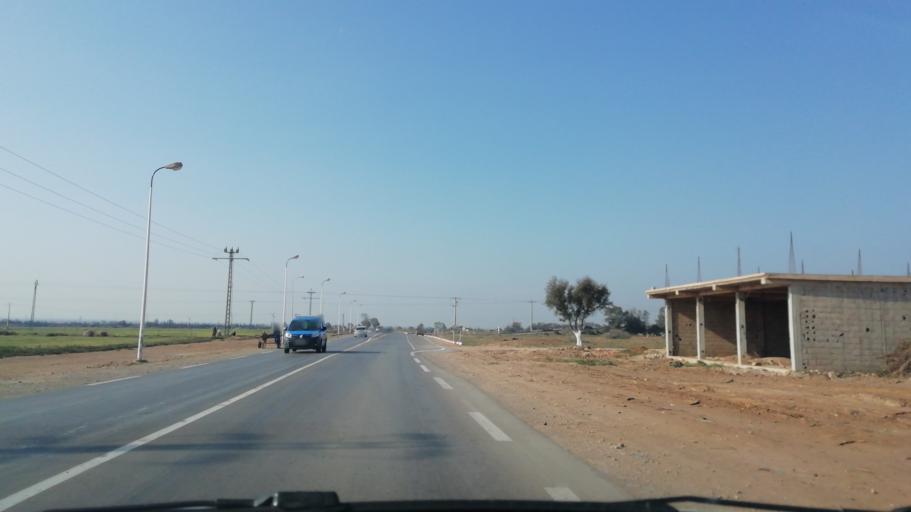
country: DZ
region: Mostaganem
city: Mostaganem
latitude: 35.7356
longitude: -0.0332
